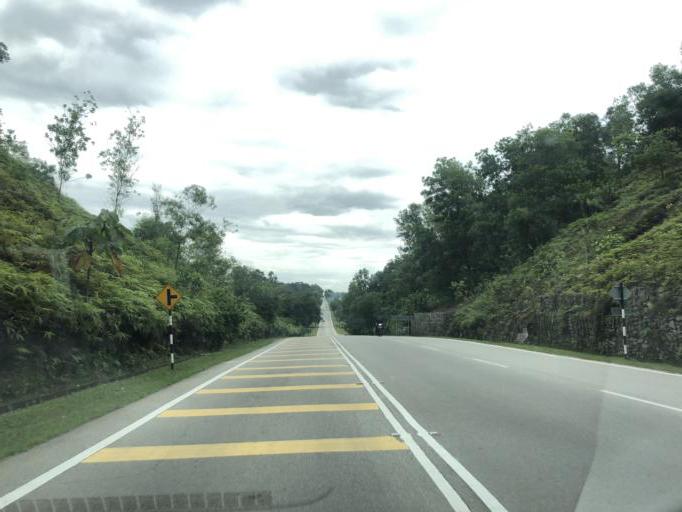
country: MY
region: Putrajaya
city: Putrajaya
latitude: 2.9240
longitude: 101.7472
